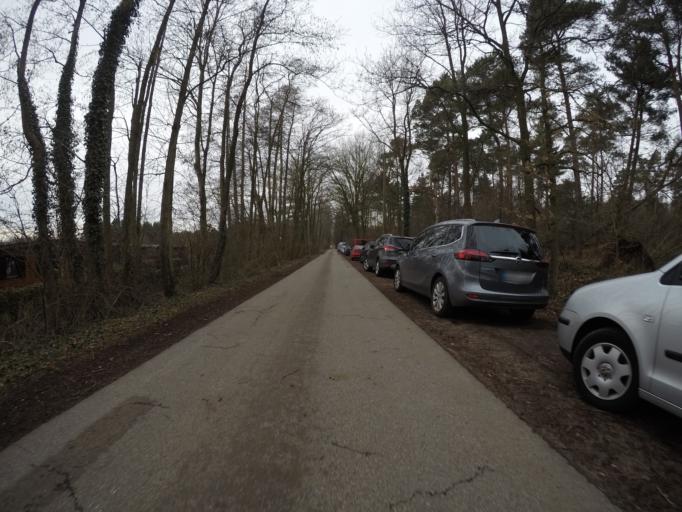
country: DE
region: North Rhine-Westphalia
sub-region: Regierungsbezirk Dusseldorf
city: Bocholt
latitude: 51.7876
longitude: 6.6359
